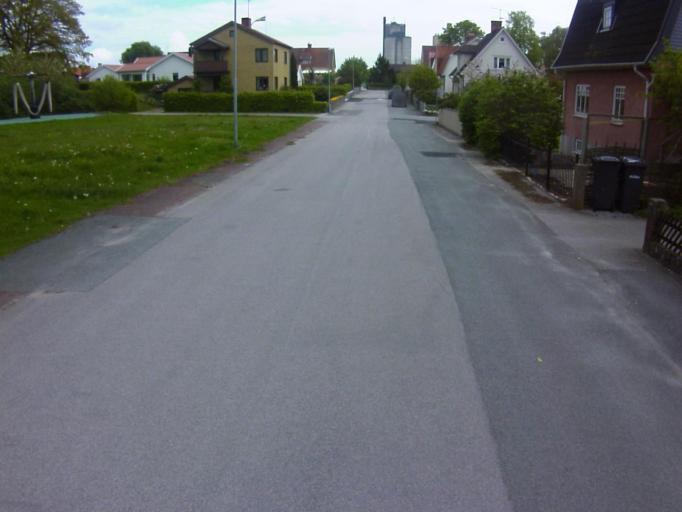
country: SE
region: Blekinge
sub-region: Solvesborgs Kommun
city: Soelvesborg
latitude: 56.0503
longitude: 14.5765
